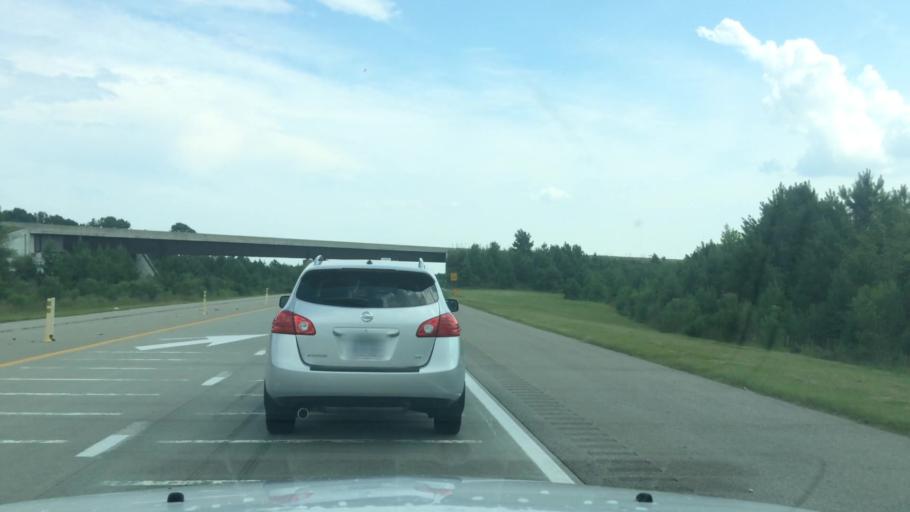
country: US
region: North Carolina
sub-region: Wake County
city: Knightdale
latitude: 35.7707
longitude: -78.5066
